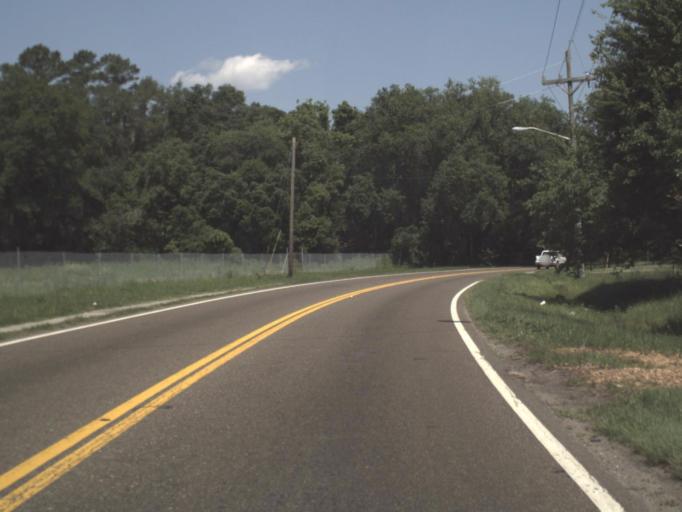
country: US
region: Florida
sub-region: Duval County
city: Jacksonville
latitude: 30.3661
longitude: -81.7426
